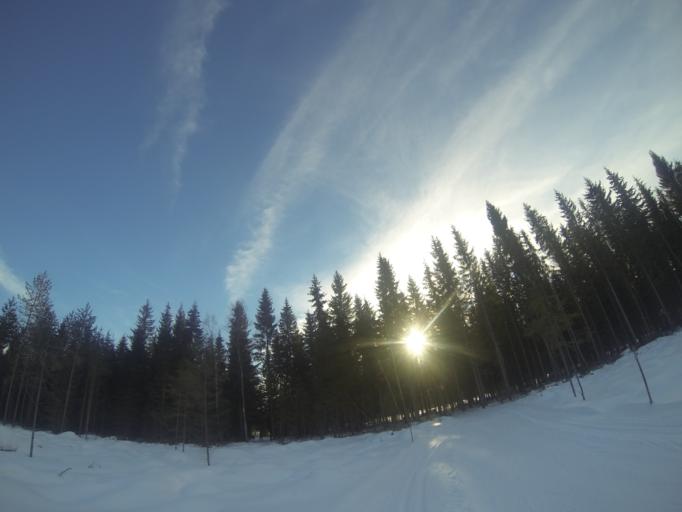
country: FI
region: Southern Savonia
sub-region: Savonlinna
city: Savonlinna
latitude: 61.9347
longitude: 28.9119
